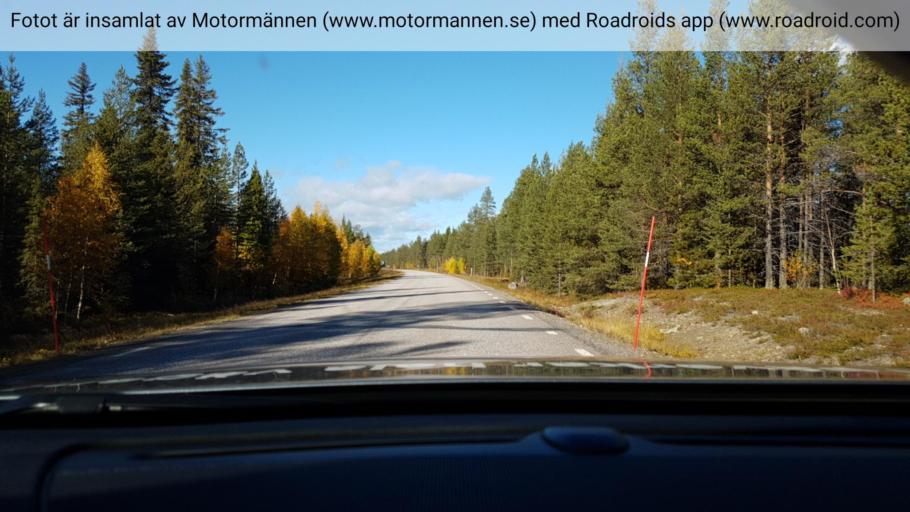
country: SE
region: Norrbotten
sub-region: Arvidsjaurs Kommun
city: Arvidsjaur
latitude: 65.6790
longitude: 18.8240
